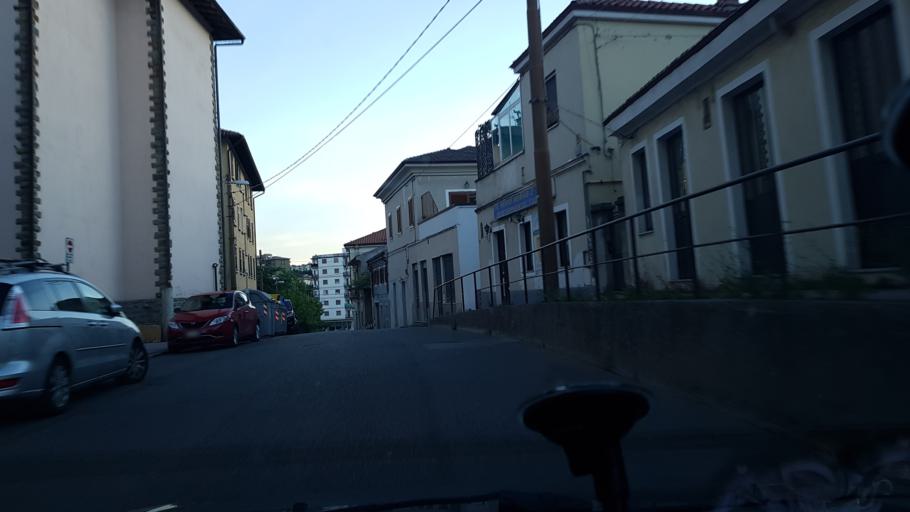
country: IT
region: Friuli Venezia Giulia
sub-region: Provincia di Trieste
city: Trieste
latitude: 45.6242
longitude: 13.7962
